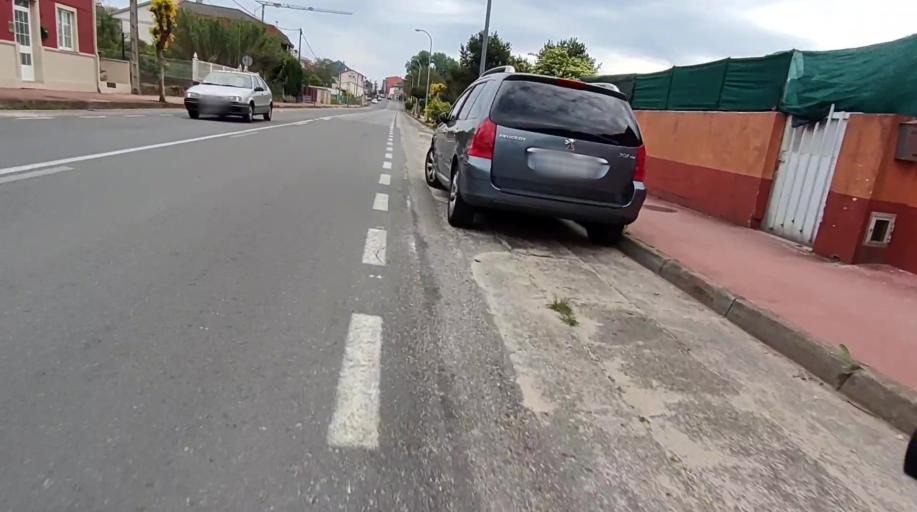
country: ES
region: Galicia
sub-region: Provincia da Coruna
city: Boiro
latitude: 42.6291
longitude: -8.8737
